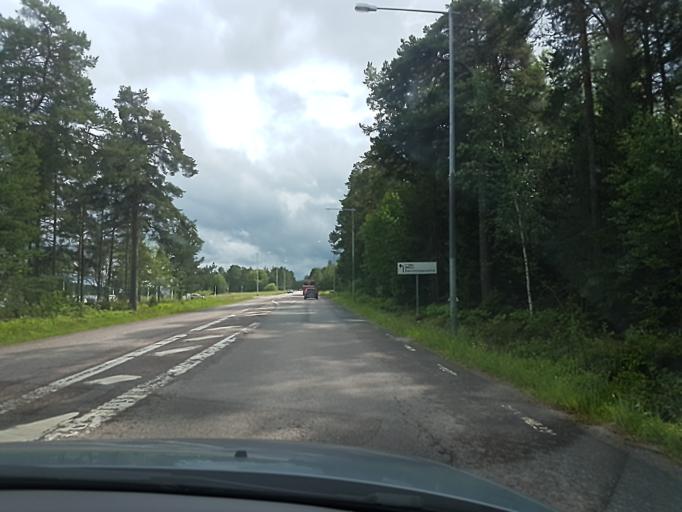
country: SE
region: Uppsala
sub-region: Osthammars Kommun
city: OEsthammar
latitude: 60.2504
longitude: 18.3476
